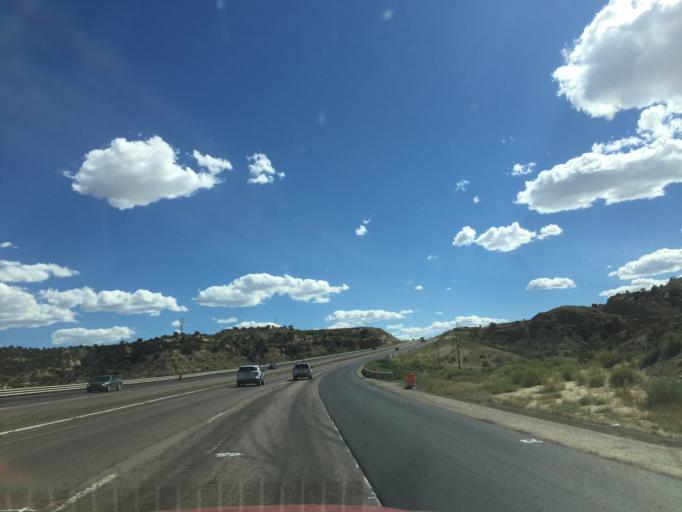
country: US
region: New Mexico
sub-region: McKinley County
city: Twin Lakes
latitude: 35.6536
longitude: -108.7684
